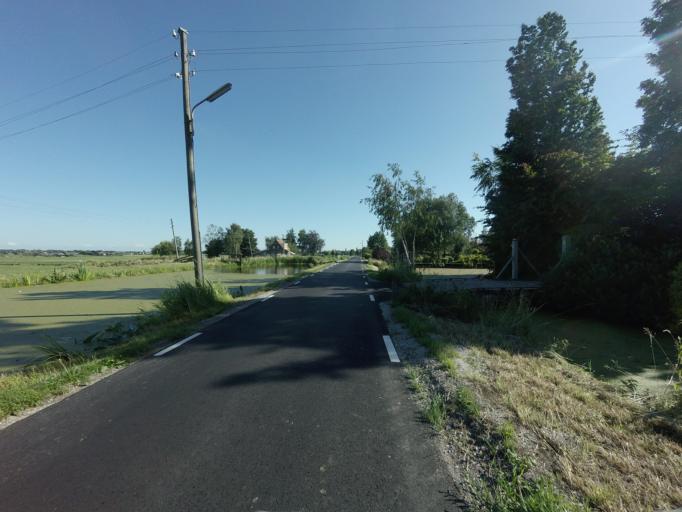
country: NL
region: South Holland
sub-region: Gemeente Waddinxveen
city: Oranjewijk
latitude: 52.0531
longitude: 4.6802
